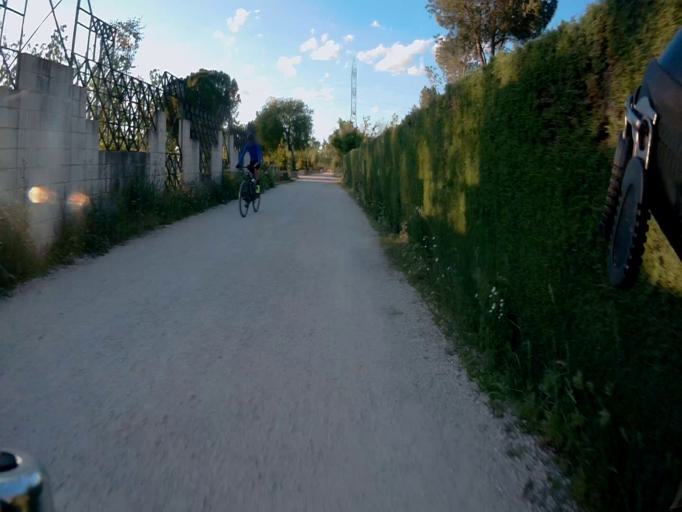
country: ES
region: Madrid
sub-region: Provincia de Madrid
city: Alcorcon
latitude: 40.3239
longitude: -3.8033
